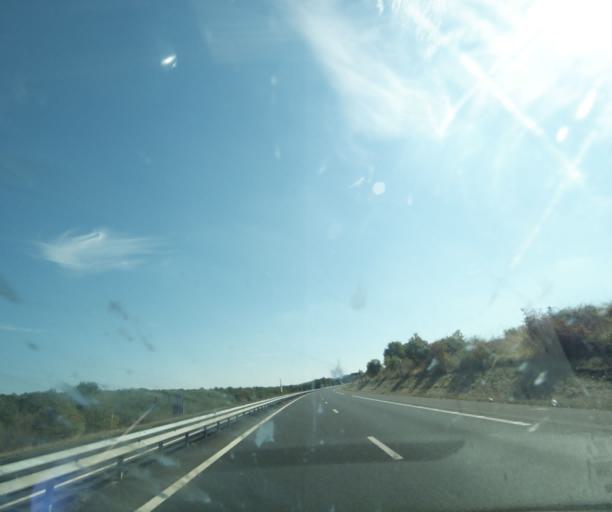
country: FR
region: Limousin
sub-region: Departement de la Correze
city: Cosnac
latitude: 45.0221
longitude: 1.5340
